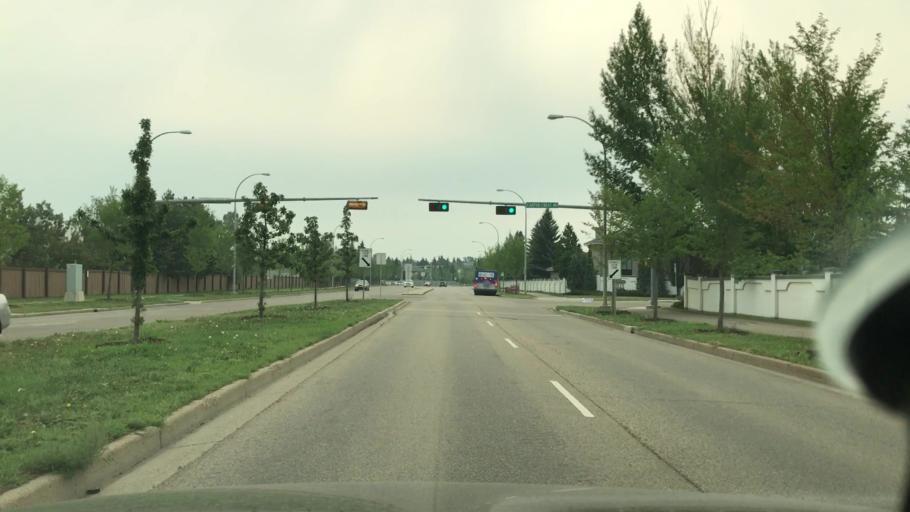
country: CA
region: Alberta
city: Edmonton
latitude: 53.4679
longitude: -113.5790
